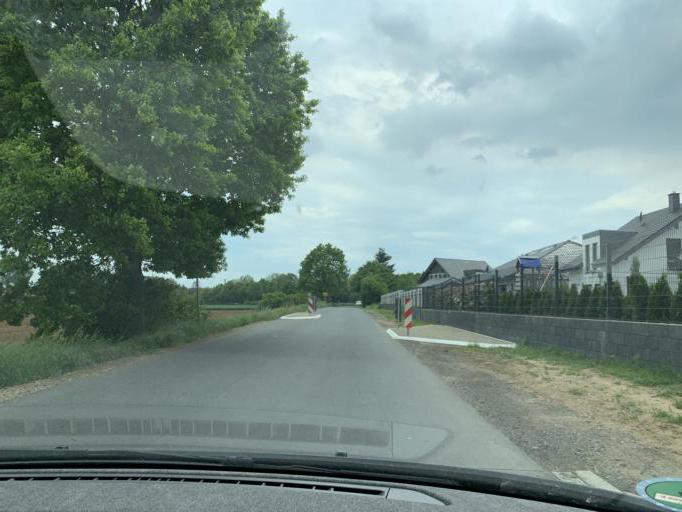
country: DE
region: North Rhine-Westphalia
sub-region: Regierungsbezirk Koln
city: Norvenich
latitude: 50.8009
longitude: 6.6379
